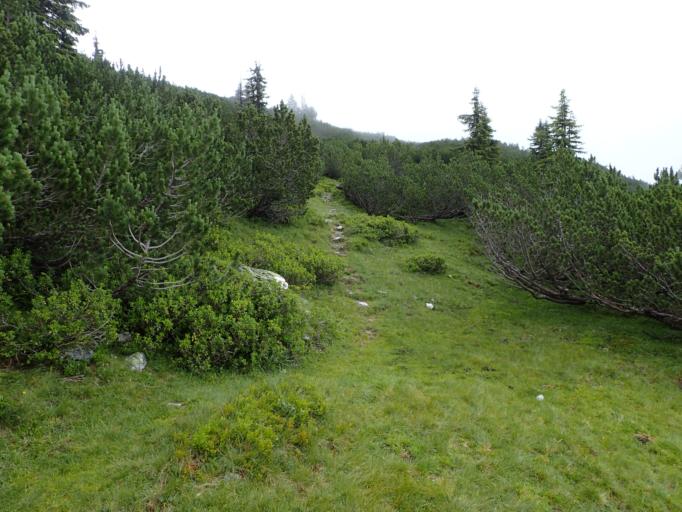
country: AT
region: Salzburg
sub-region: Politischer Bezirk Sankt Johann im Pongau
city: Untertauern
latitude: 47.3053
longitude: 13.4747
